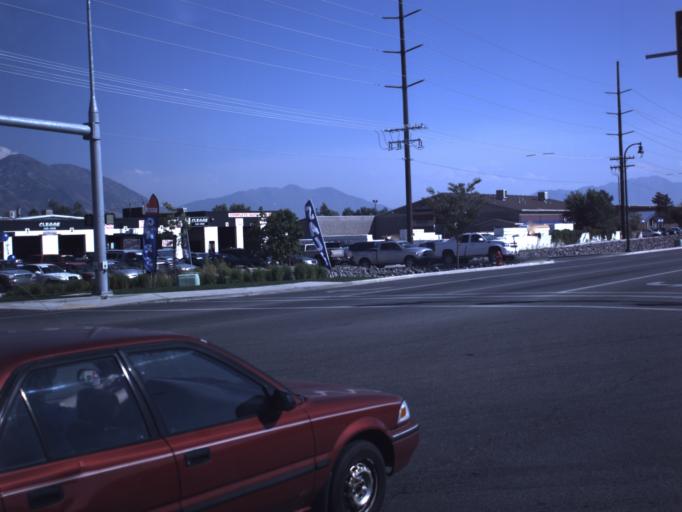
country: US
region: Utah
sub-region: Utah County
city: Orem
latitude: 40.2972
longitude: -111.7342
